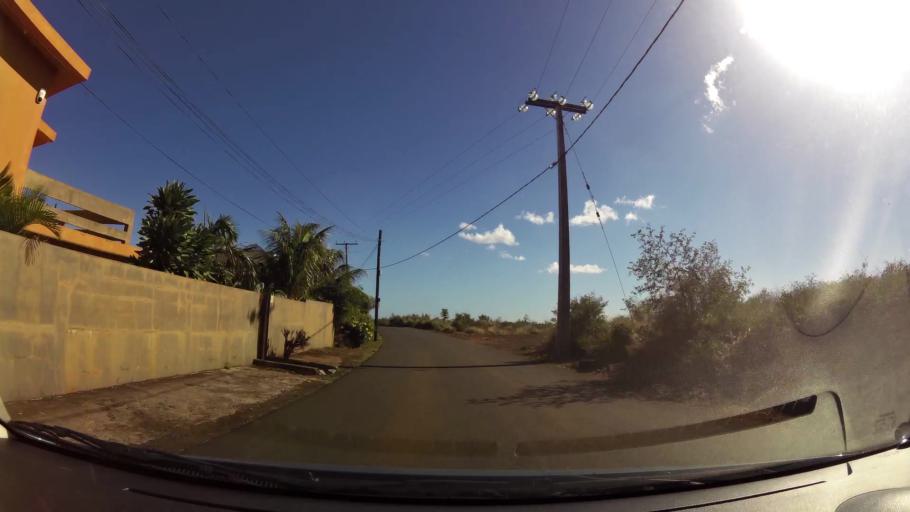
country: MU
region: Black River
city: Flic en Flac
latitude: -20.2749
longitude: 57.3768
